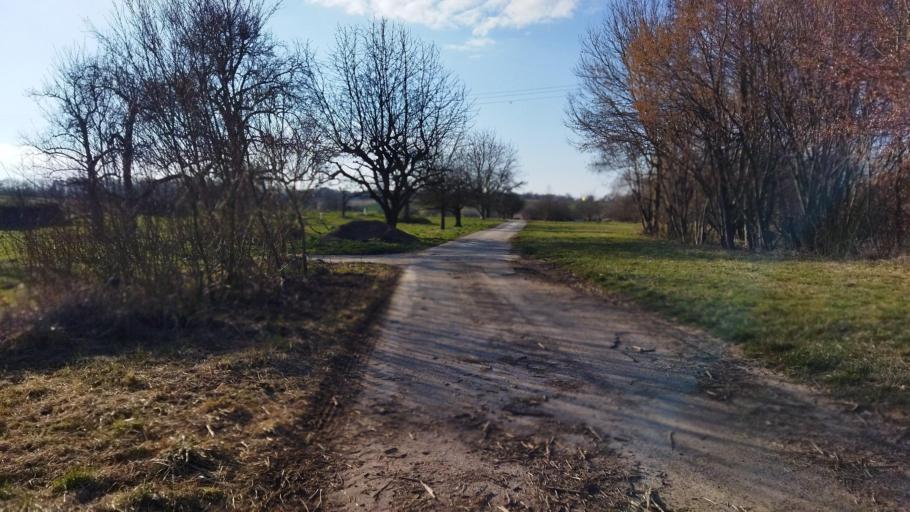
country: DE
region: Baden-Wuerttemberg
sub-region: Regierungsbezirk Stuttgart
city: Mundelsheim
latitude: 49.0213
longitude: 9.1958
